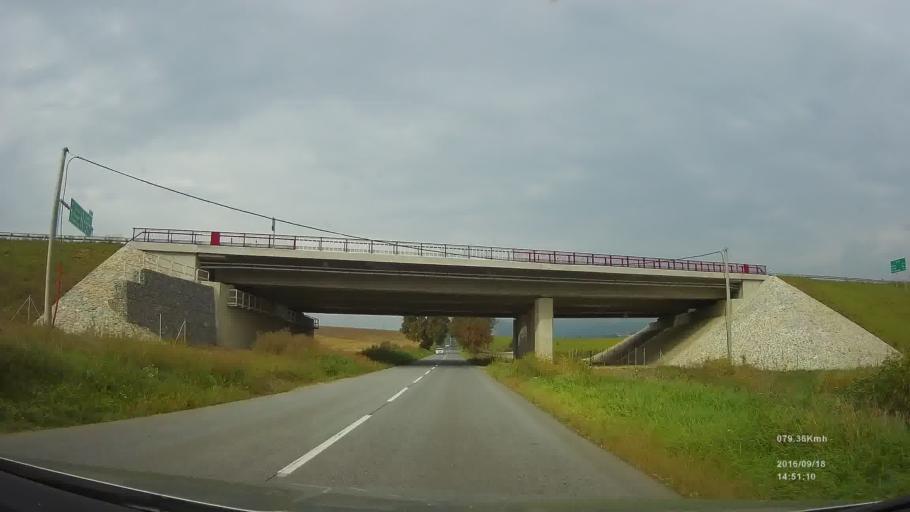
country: SK
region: Presovsky
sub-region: Okres Presov
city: Levoca
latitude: 49.0049
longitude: 20.5844
